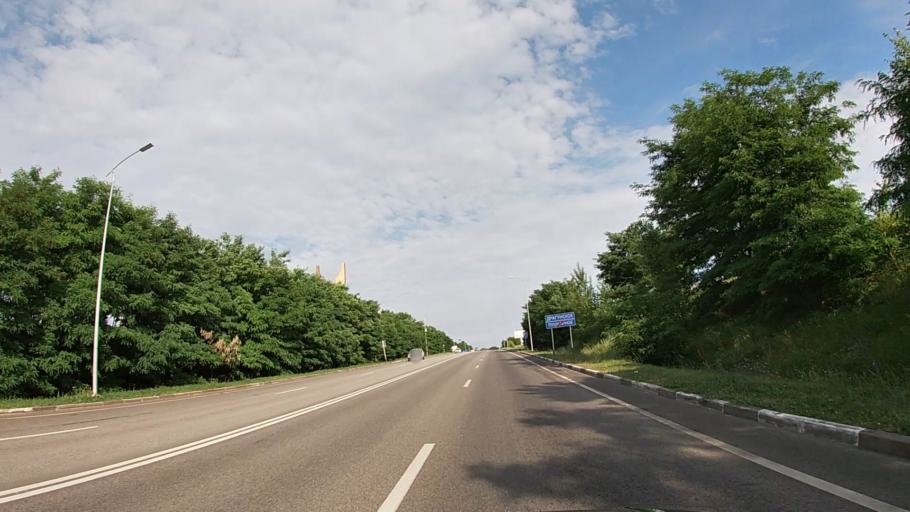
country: RU
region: Belgorod
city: Severnyy
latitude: 50.6367
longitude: 36.4494
